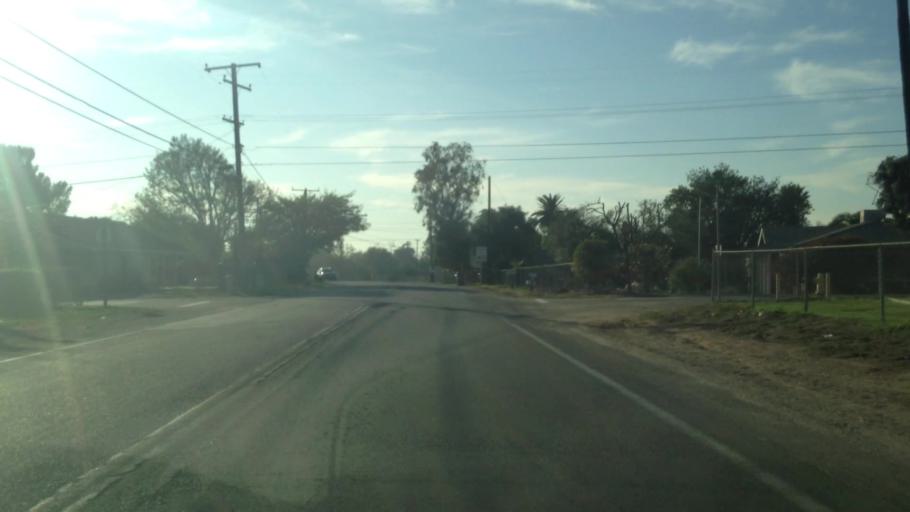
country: US
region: California
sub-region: Riverside County
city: Mira Loma
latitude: 33.9720
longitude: -117.5294
